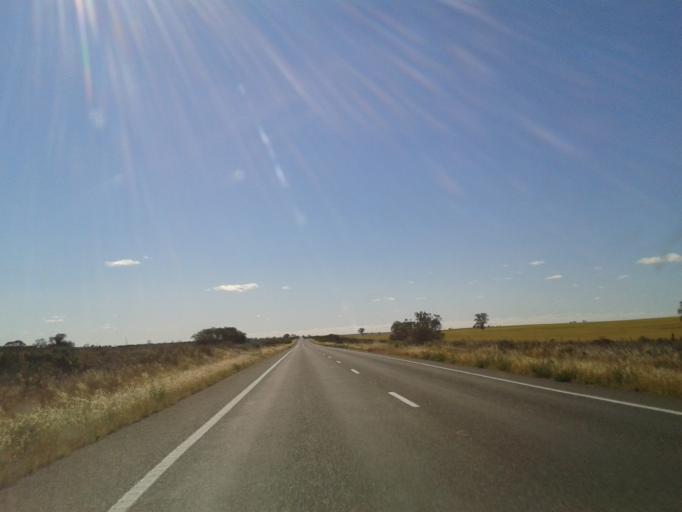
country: AU
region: South Australia
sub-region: Renmark Paringa
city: Renmark
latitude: -34.2750
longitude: 141.1468
